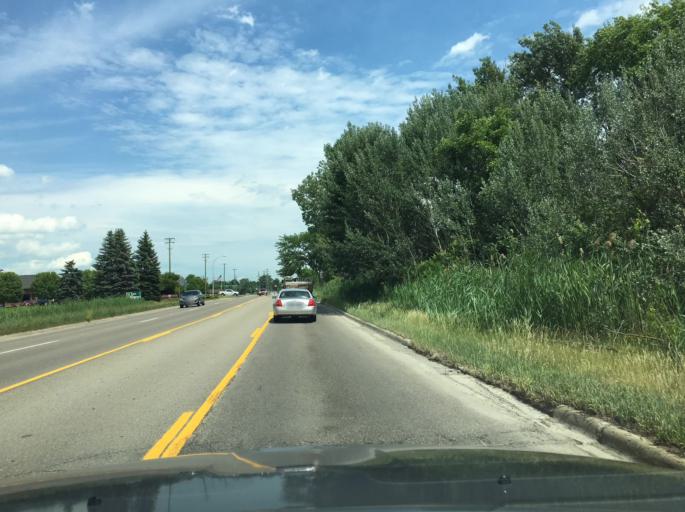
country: US
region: Michigan
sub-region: Macomb County
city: Shelby
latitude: 42.7140
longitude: -83.0205
